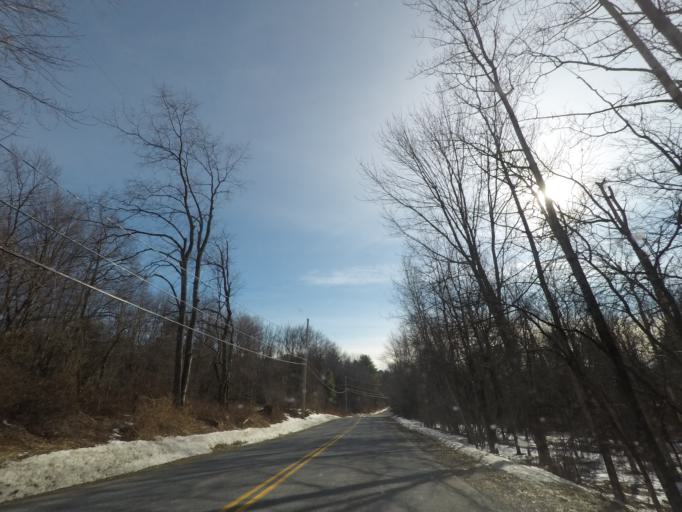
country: US
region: New York
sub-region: Rensselaer County
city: Poestenkill
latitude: 42.6989
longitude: -73.4216
